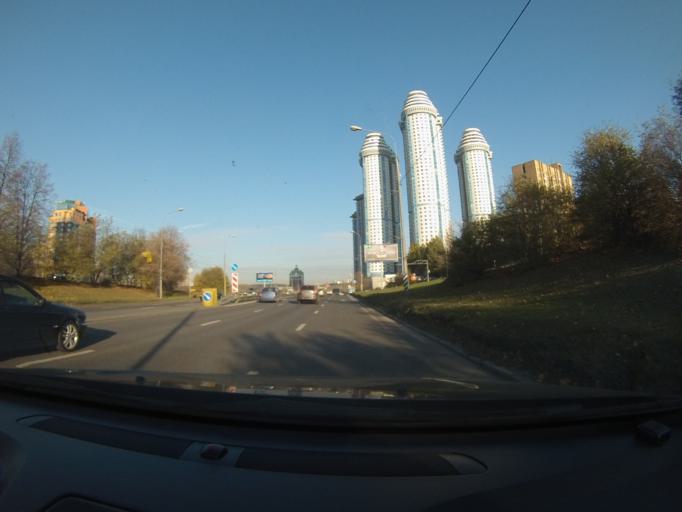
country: RU
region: Moskovskaya
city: Kastanayevo
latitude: 55.7114
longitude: 37.5057
